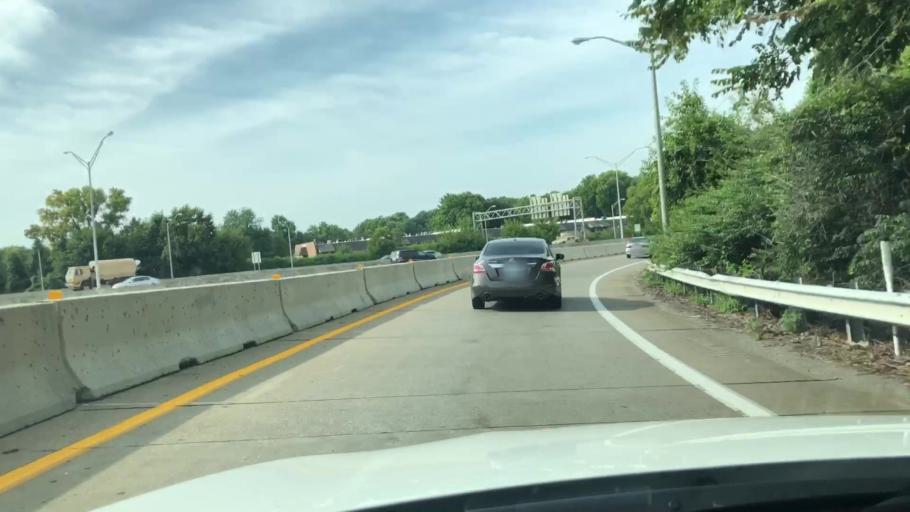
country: US
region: Kentucky
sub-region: Jefferson County
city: Saint Regis Park
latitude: 38.2279
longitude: -85.6386
